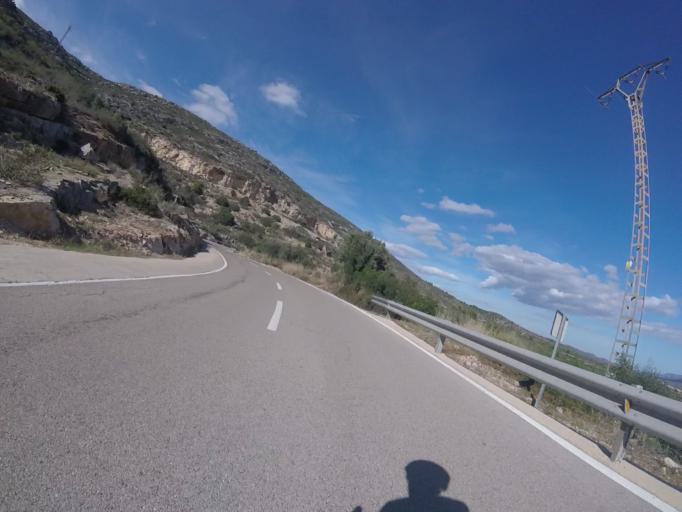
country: ES
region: Valencia
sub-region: Provincia de Castello
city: Alcala de Xivert
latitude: 40.2975
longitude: 0.1869
